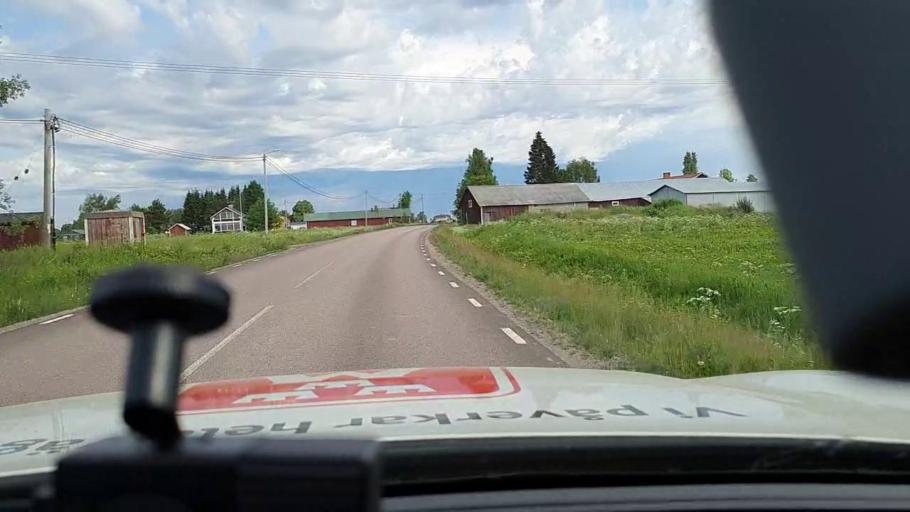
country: SE
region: Norrbotten
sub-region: Bodens Kommun
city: Saevast
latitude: 65.7020
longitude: 21.7698
